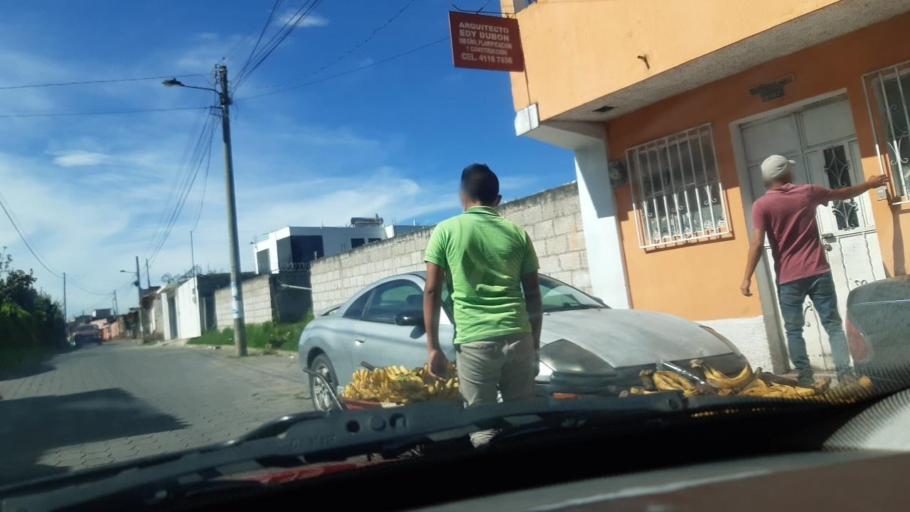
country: GT
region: Quetzaltenango
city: Salcaja
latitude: 14.8846
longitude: -91.4534
